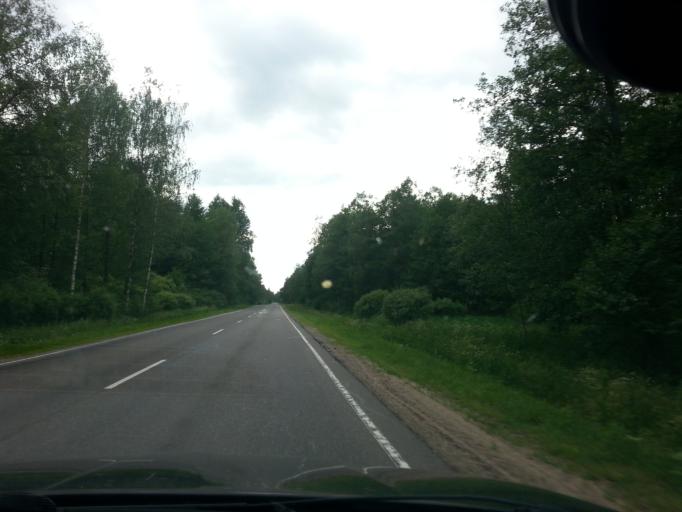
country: BY
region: Minsk
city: Svir
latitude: 54.8501
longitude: 26.2295
